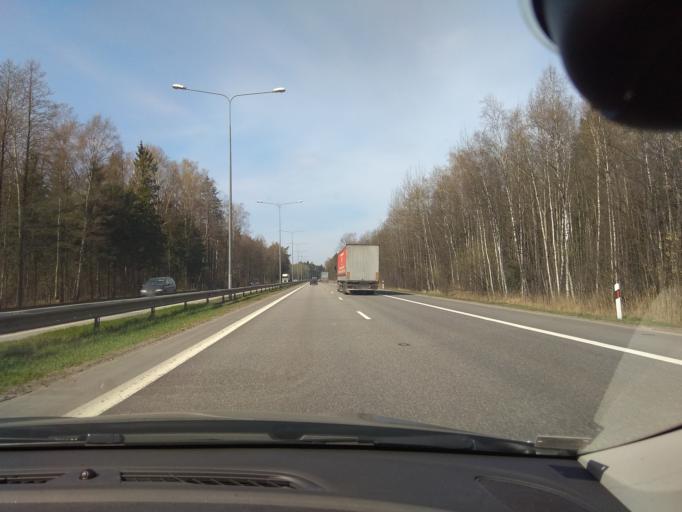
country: LT
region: Kauno apskritis
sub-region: Kauno rajonas
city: Karmelava
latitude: 54.8874
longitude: 24.1764
